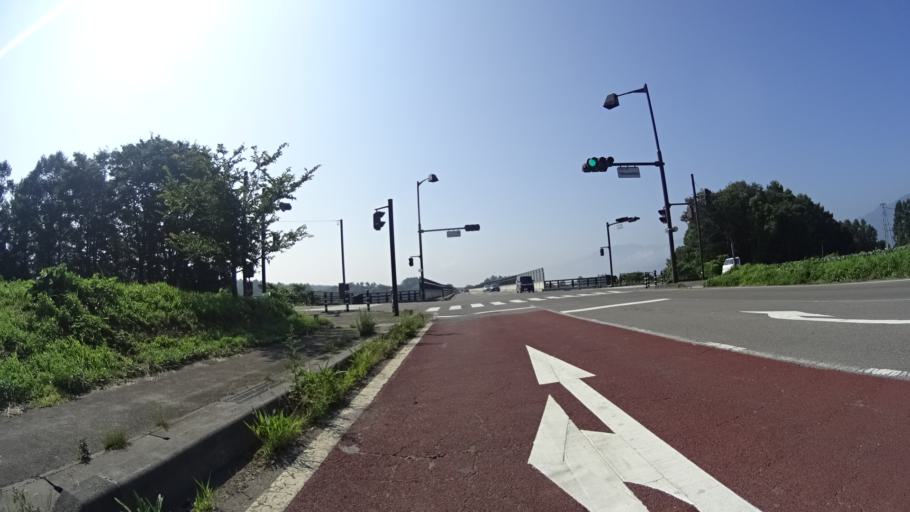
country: JP
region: Nagano
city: Chino
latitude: 35.9343
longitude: 138.2619
